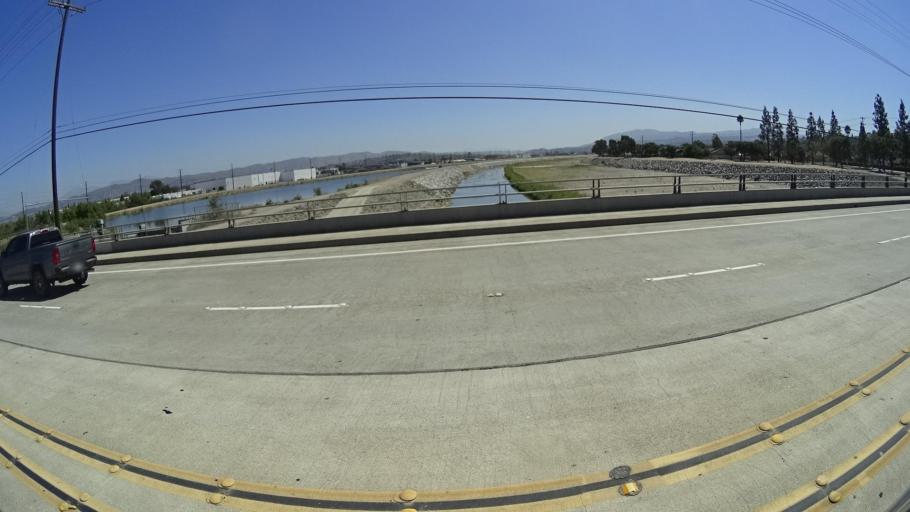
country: US
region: California
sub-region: Orange County
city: Yorba Linda
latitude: 33.8551
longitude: -117.8177
